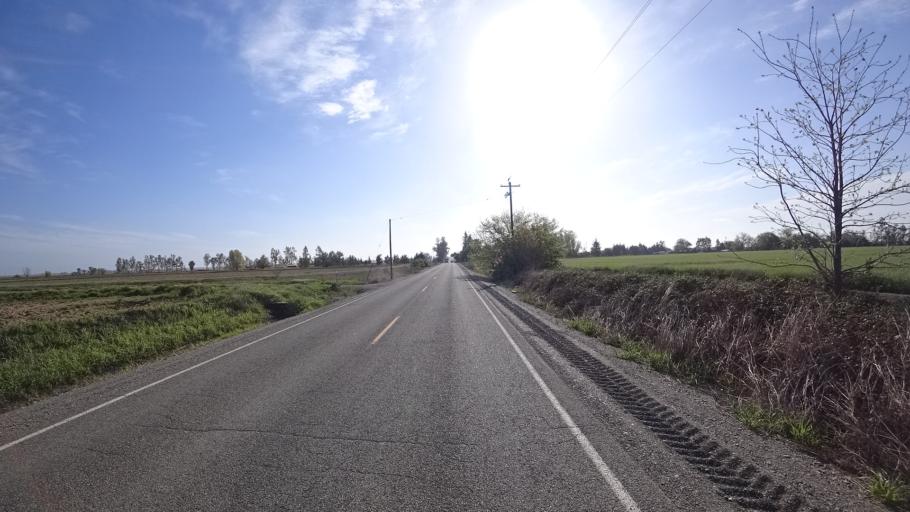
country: US
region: California
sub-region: Glenn County
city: Willows
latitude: 39.5825
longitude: -122.0420
